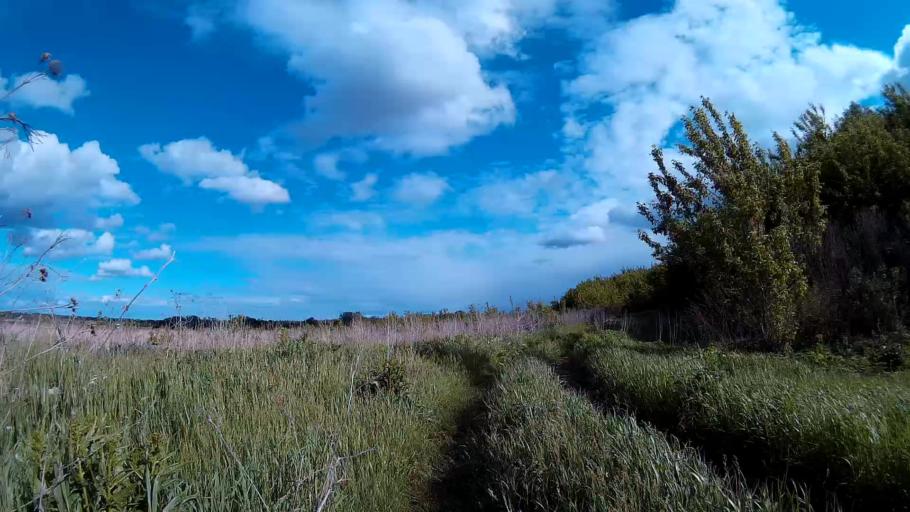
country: RU
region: Ulyanovsk
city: Novoul'yanovsk
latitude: 54.2166
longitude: 48.2597
